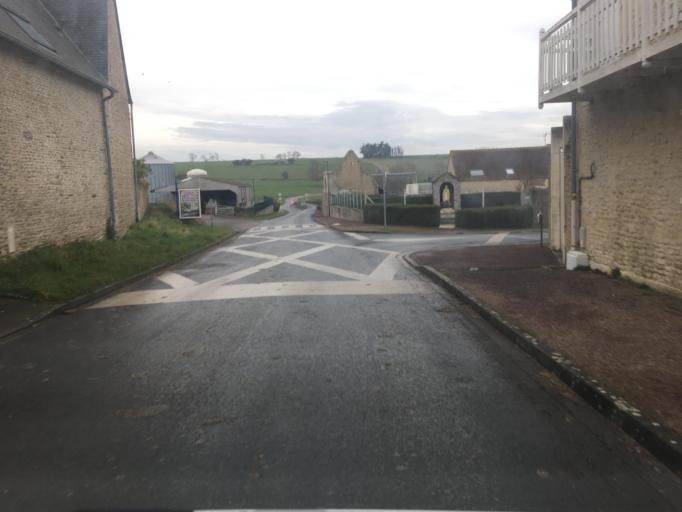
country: FR
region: Lower Normandy
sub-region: Departement du Calvados
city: Ver-sur-Mer
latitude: 49.3310
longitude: -0.6047
